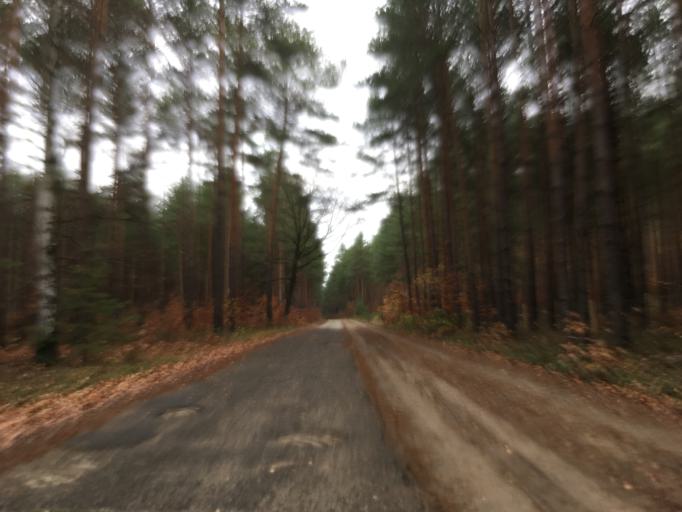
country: DE
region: Brandenburg
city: Jamlitz
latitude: 52.0642
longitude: 14.4826
